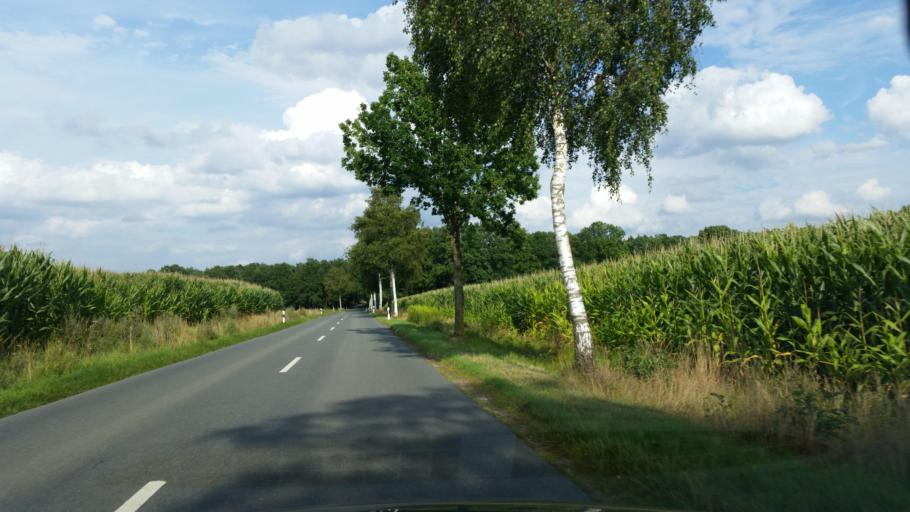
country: DE
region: Lower Saxony
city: Schneverdingen
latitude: 53.0611
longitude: 9.7780
